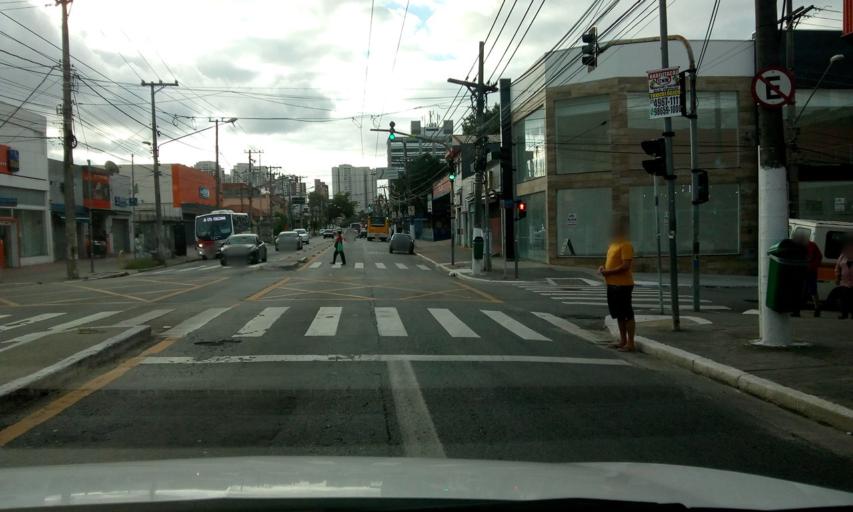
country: BR
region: Sao Paulo
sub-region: Sao Caetano Do Sul
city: Sao Caetano do Sul
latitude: -23.5475
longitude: -46.5401
